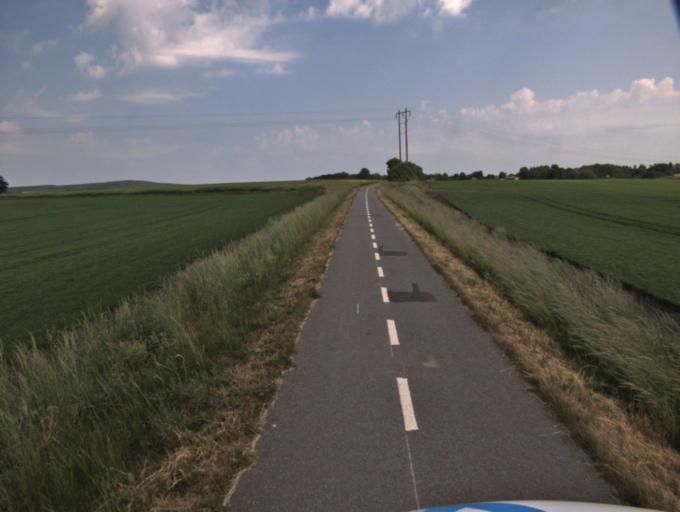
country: SE
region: Skane
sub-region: Kristianstads Kommun
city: Kristianstad
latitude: 56.0684
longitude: 14.1944
